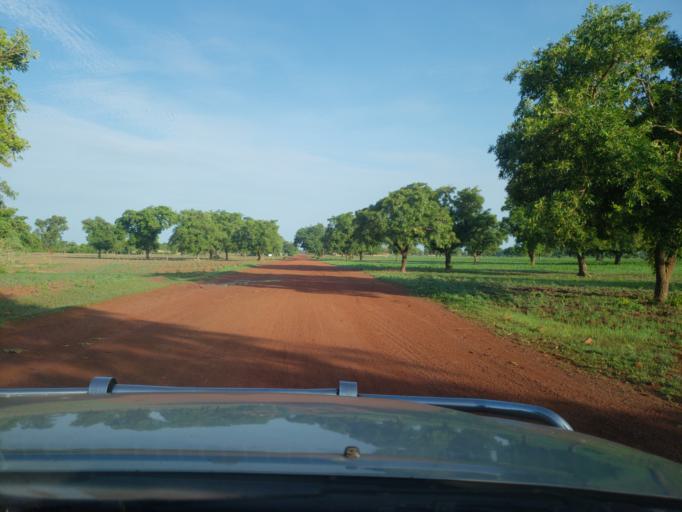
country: ML
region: Sikasso
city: Koutiala
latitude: 12.4155
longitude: -5.5686
